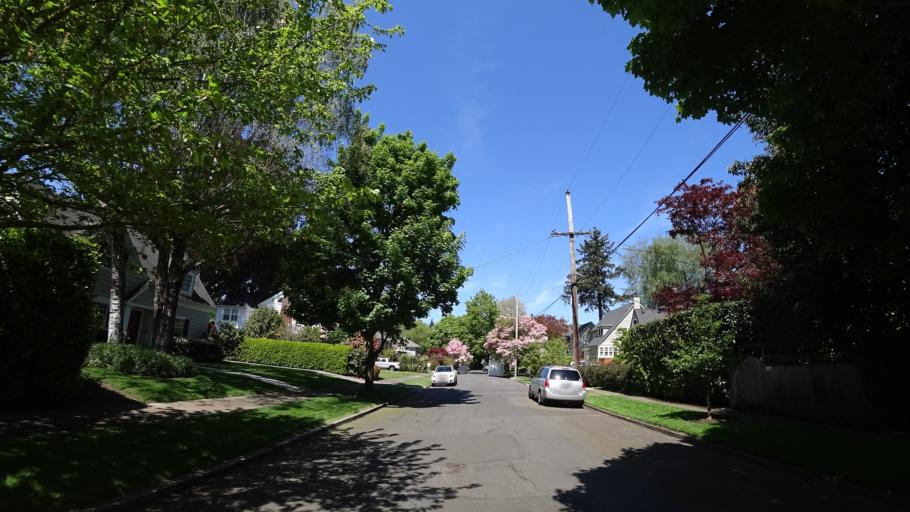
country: US
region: Oregon
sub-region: Clackamas County
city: Milwaukie
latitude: 45.4761
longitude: -122.6324
